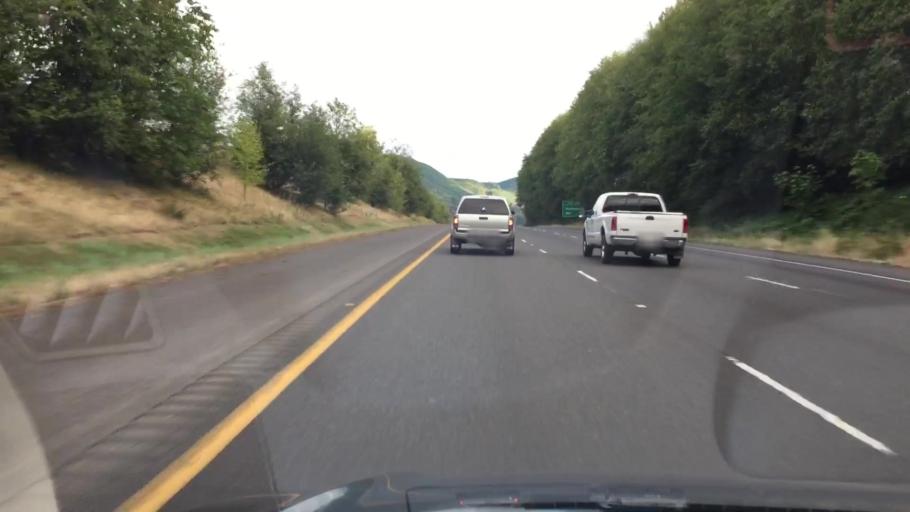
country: US
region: Washington
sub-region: Cowlitz County
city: Castle Rock
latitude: 46.2669
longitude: -122.8926
